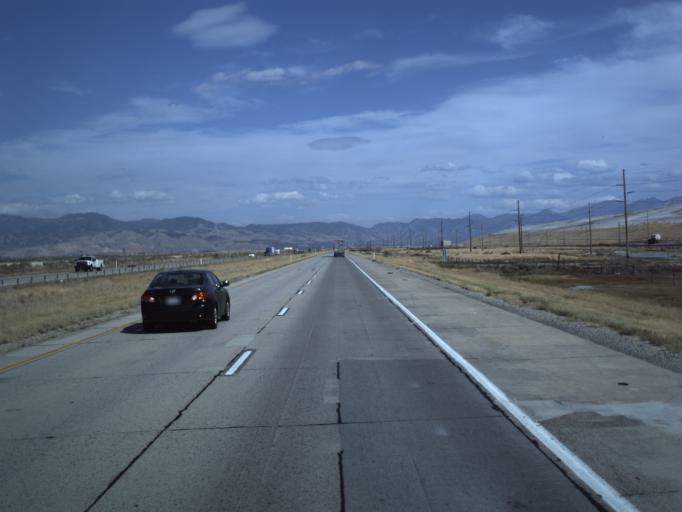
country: US
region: Utah
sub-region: Salt Lake County
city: Magna
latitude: 40.7707
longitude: -112.1268
